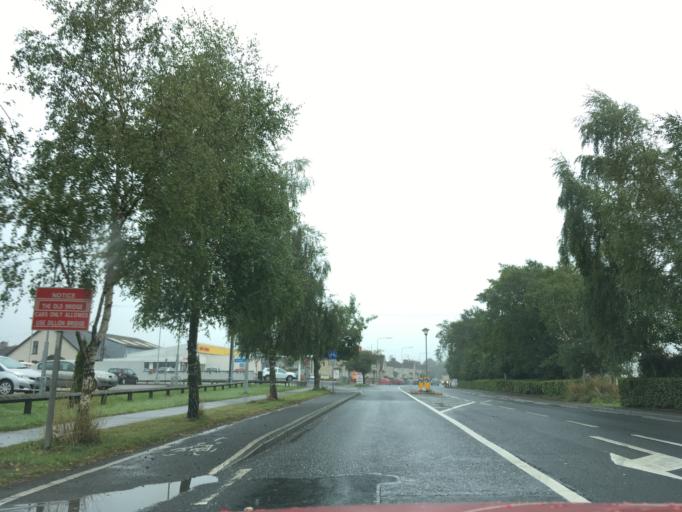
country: IE
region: Munster
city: Carrick-on-Suir
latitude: 52.3487
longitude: -7.4249
